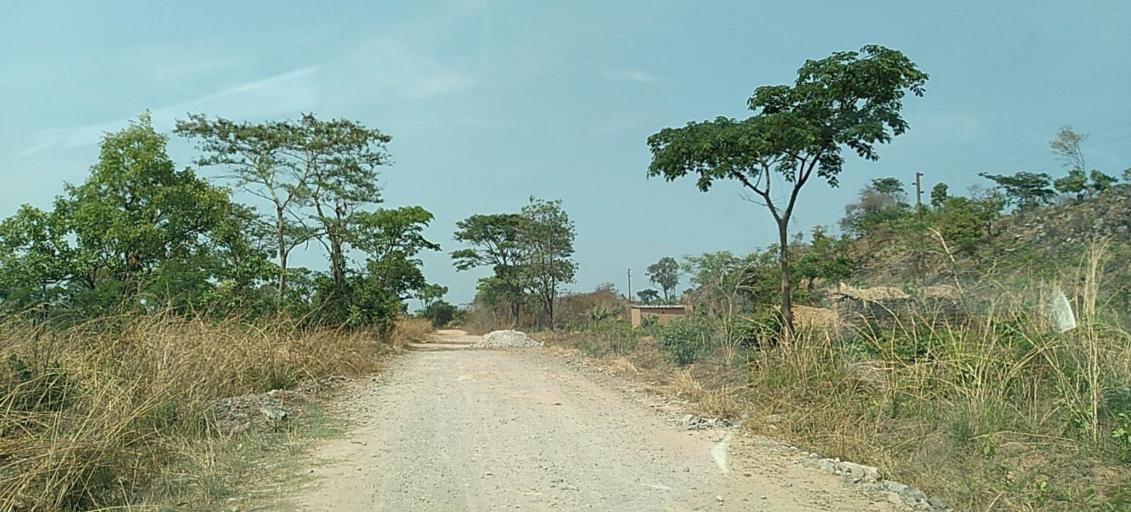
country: ZM
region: Copperbelt
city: Chililabombwe
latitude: -12.3317
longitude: 27.7305
